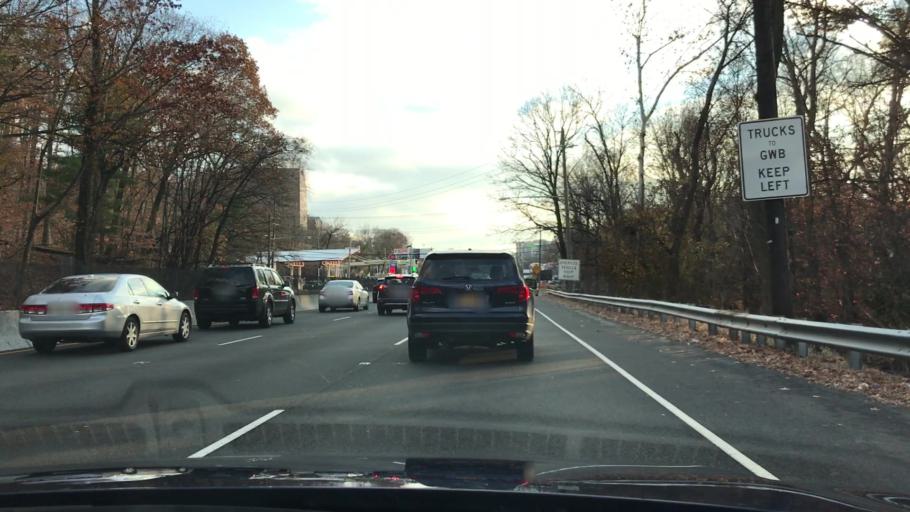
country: US
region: New Jersey
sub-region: Bergen County
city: Leonia
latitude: 40.8700
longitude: -73.9727
